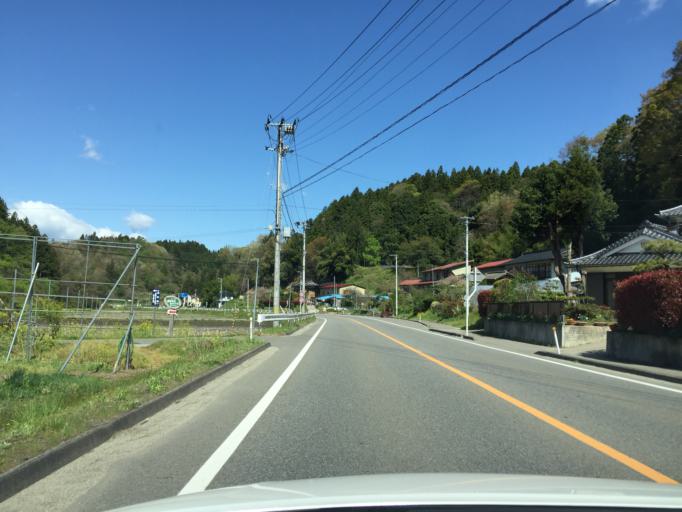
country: JP
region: Fukushima
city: Funehikimachi-funehiki
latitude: 37.5366
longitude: 140.5903
